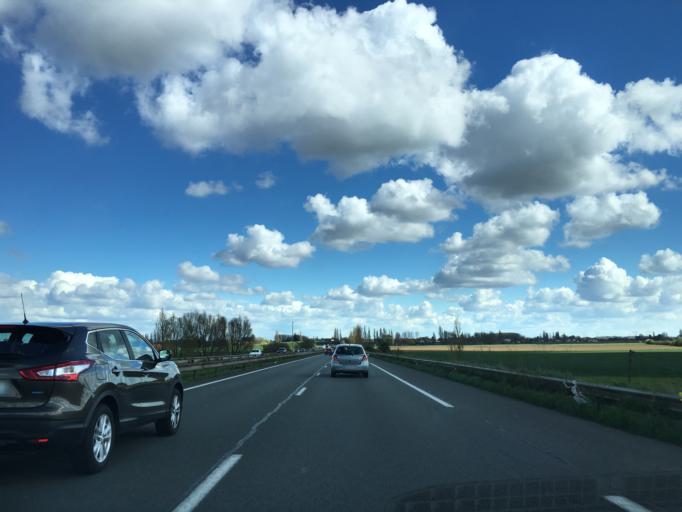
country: FR
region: Nord-Pas-de-Calais
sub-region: Departement du Nord
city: Erquinghem-Lys
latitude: 50.6765
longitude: 2.8593
